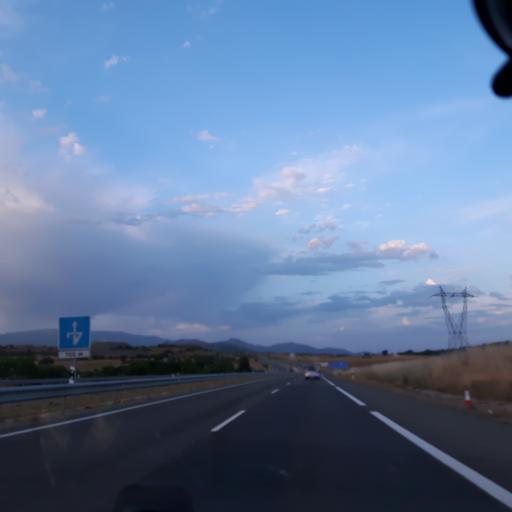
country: ES
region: Castille and Leon
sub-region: Provincia de Salamanca
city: Guijuelo
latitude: 40.5324
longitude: -5.6672
